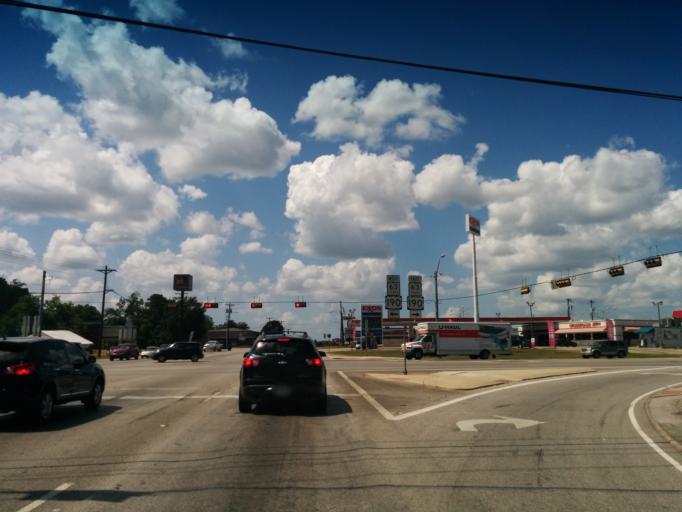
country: US
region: Texas
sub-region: Jasper County
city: Jasper
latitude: 30.9107
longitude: -93.9954
